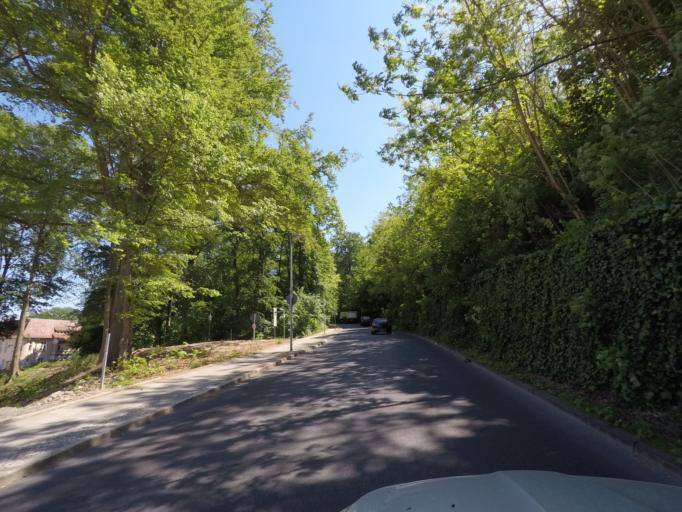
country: DE
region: Brandenburg
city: Eberswalde
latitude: 52.8290
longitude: 13.8152
